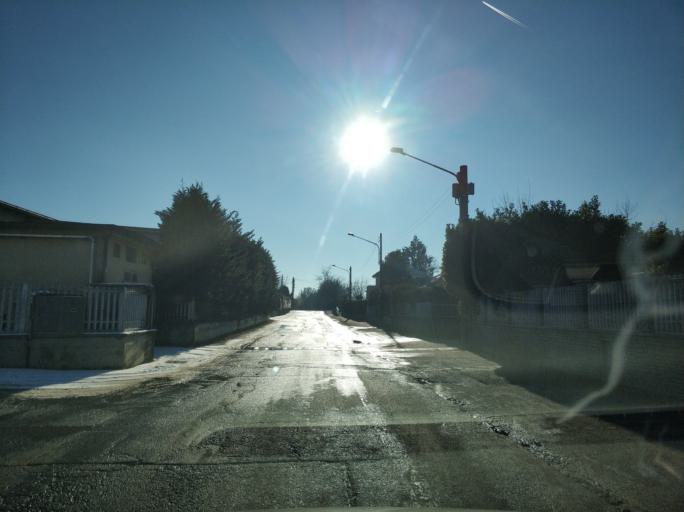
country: IT
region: Piedmont
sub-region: Provincia di Torino
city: San Maurizio
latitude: 45.2376
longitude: 7.6347
